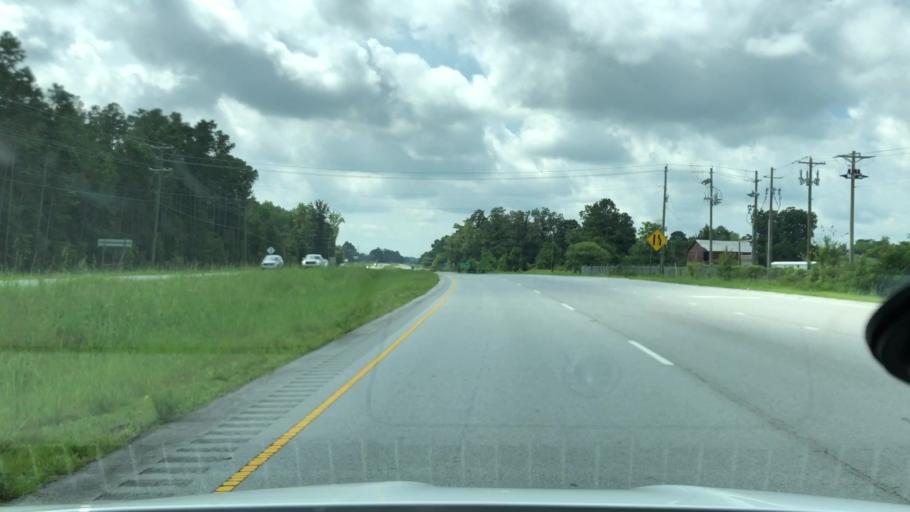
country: US
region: North Carolina
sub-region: Beaufort County
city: Washington
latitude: 35.4993
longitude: -77.1039
